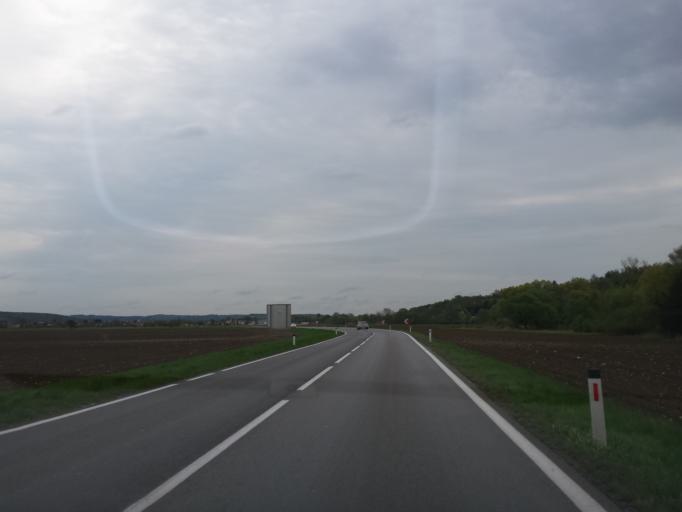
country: AT
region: Styria
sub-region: Politischer Bezirk Hartberg-Fuerstenfeld
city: Altenmarkt bei Fuerstenfeld
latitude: 47.0666
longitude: 16.0235
